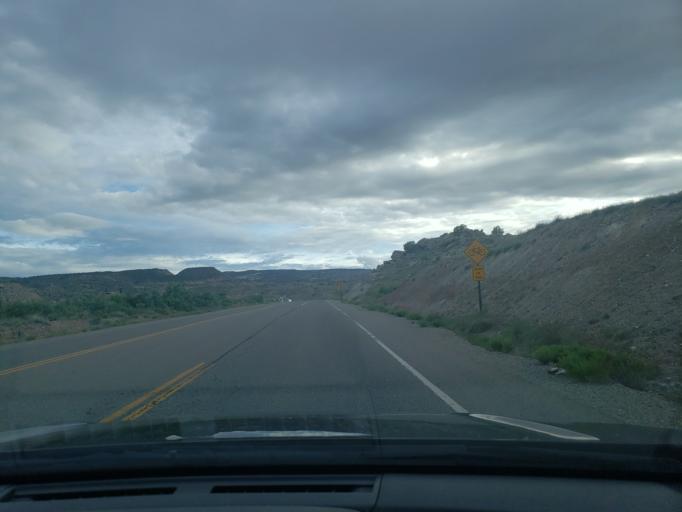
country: US
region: Colorado
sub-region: Mesa County
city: Redlands
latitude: 39.0514
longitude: -108.6047
